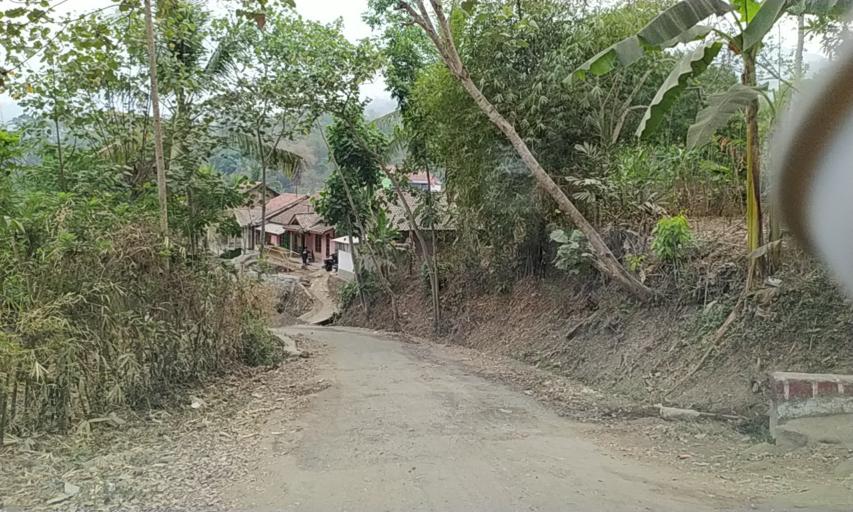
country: ID
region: Central Java
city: Bantarmangu
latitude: -7.3510
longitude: 108.8952
